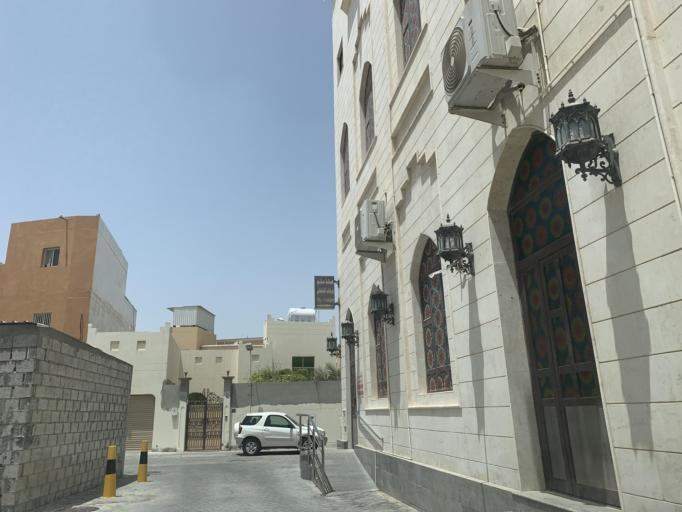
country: BH
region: Northern
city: Madinat `Isa
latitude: 26.1707
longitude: 50.5720
